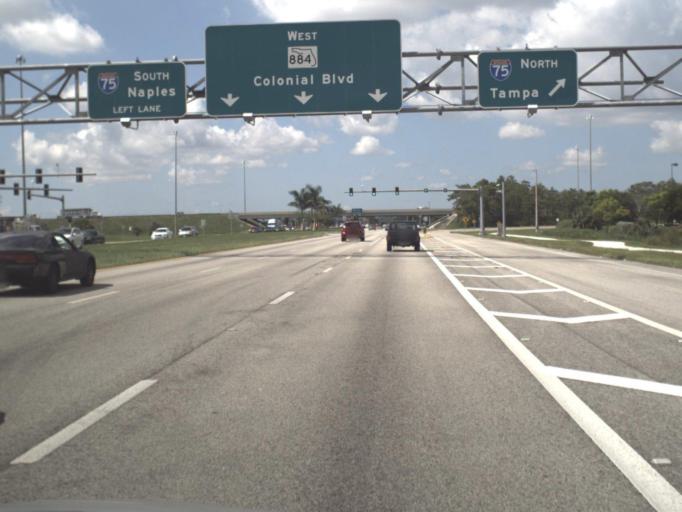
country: US
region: Florida
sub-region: Lee County
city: Fort Myers
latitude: 26.6131
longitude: -81.7991
